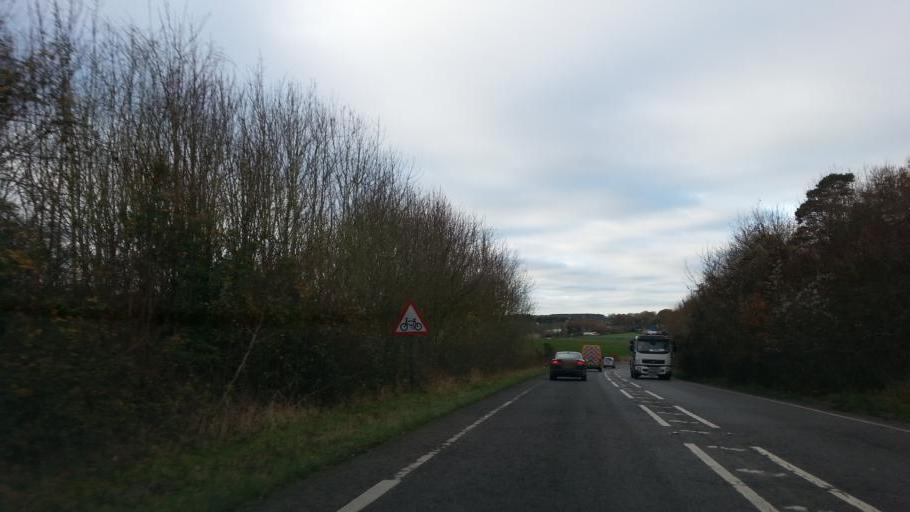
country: GB
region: England
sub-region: Suffolk
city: Botesdale
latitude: 52.3362
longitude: 0.9738
